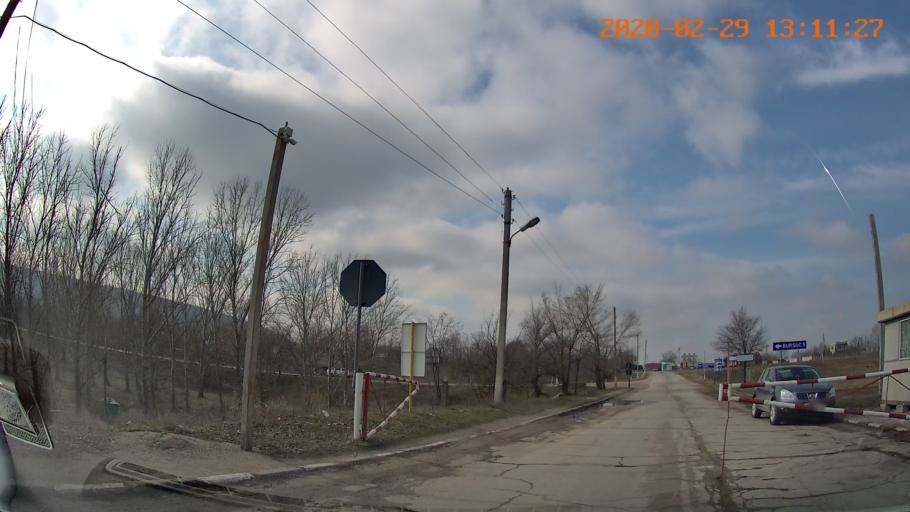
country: MD
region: Telenesti
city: Camenca
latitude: 48.0125
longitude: 28.6989
